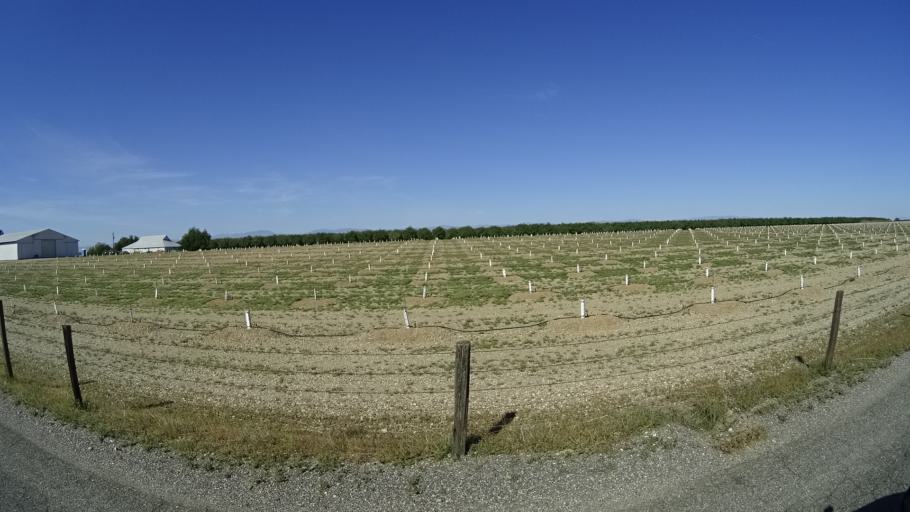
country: US
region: California
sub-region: Glenn County
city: Willows
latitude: 39.6130
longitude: -122.1565
